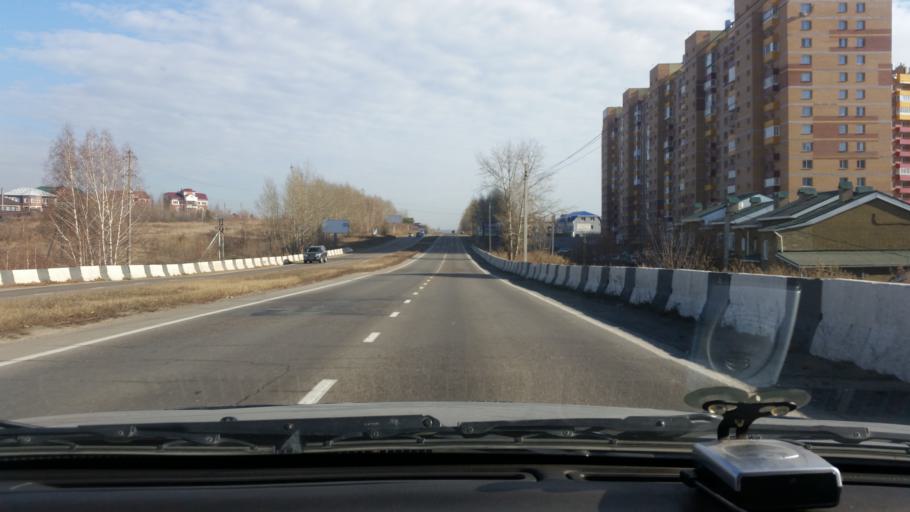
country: RU
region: Irkutsk
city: Dzerzhinsk
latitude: 52.2595
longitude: 104.3610
